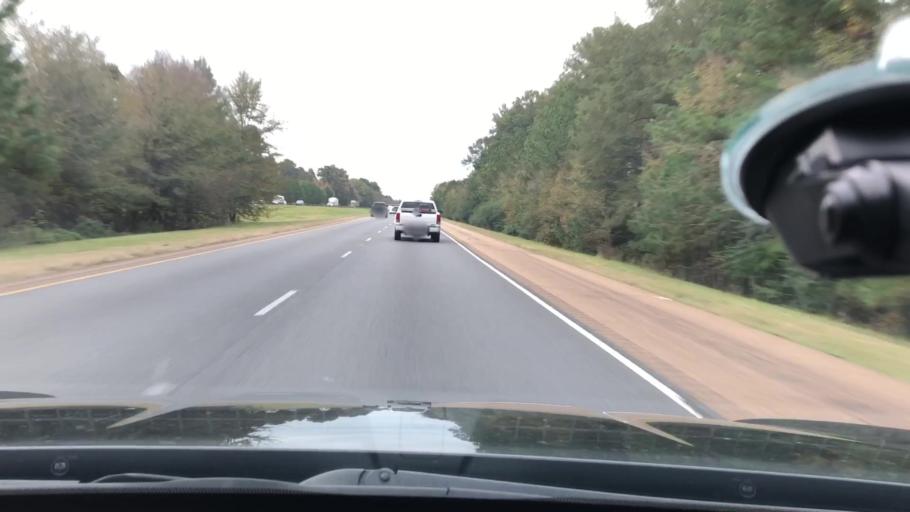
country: US
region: Arkansas
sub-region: Nevada County
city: Prescott
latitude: 33.8758
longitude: -93.3338
